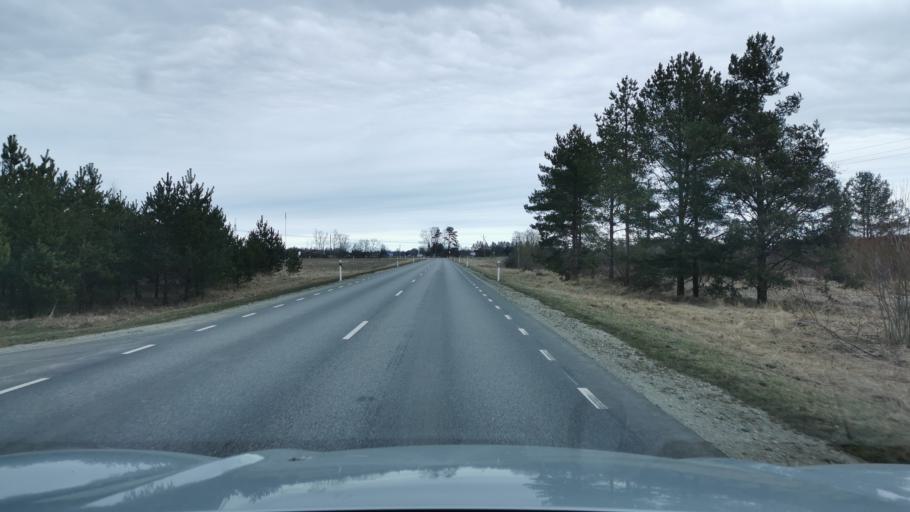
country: EE
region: Ida-Virumaa
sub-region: Puessi linn
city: Pussi
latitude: 59.3657
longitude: 27.0289
